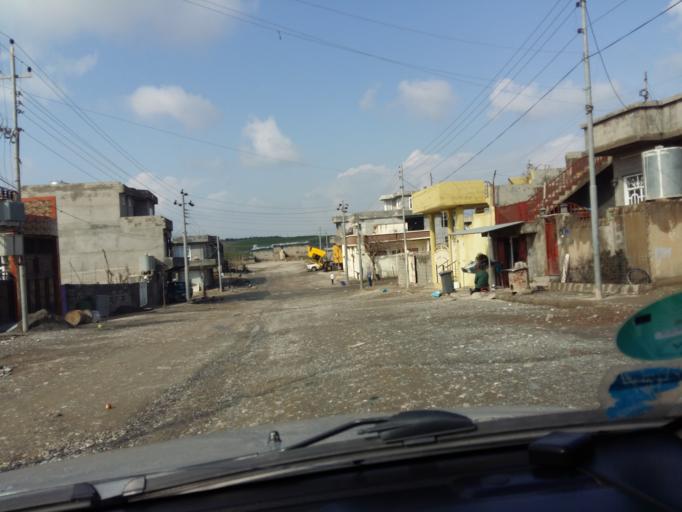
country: IQ
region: As Sulaymaniyah
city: Qeladize
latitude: 36.1937
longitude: 45.1243
